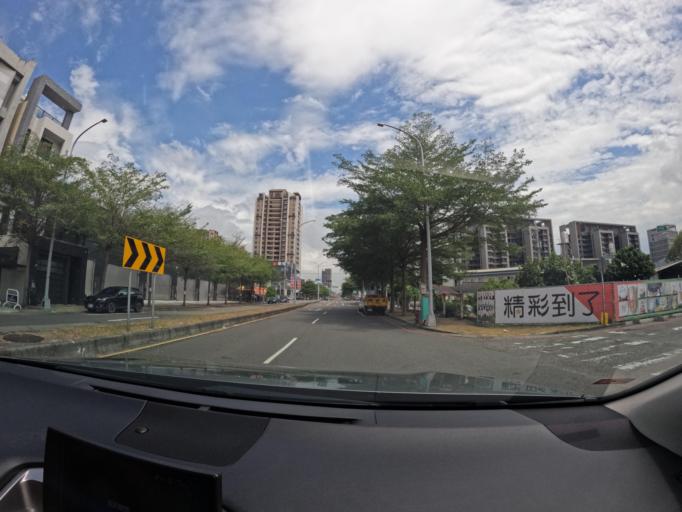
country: TW
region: Taiwan
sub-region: Taichung City
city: Taichung
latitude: 24.1396
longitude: 120.6259
